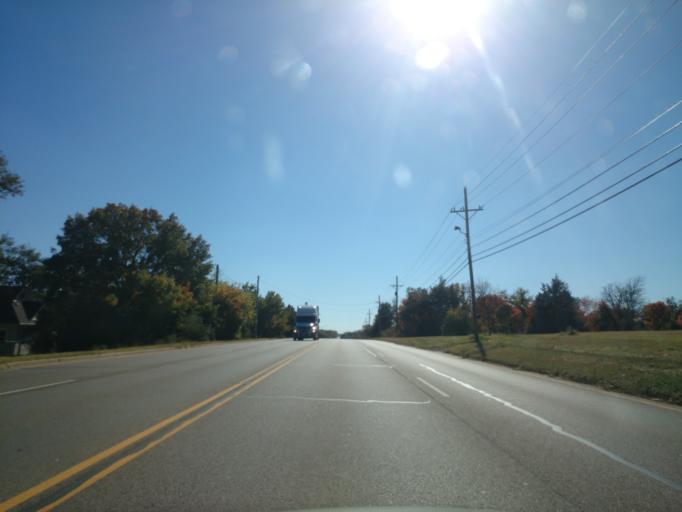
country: US
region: Oklahoma
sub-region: Payne County
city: Stillwater
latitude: 36.1655
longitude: -97.0697
